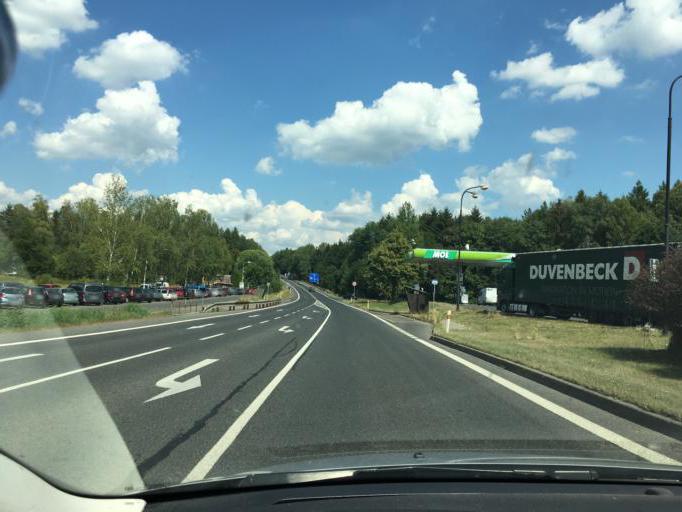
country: CZ
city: Jablonne v Podjestedi
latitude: 50.7711
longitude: 14.7610
